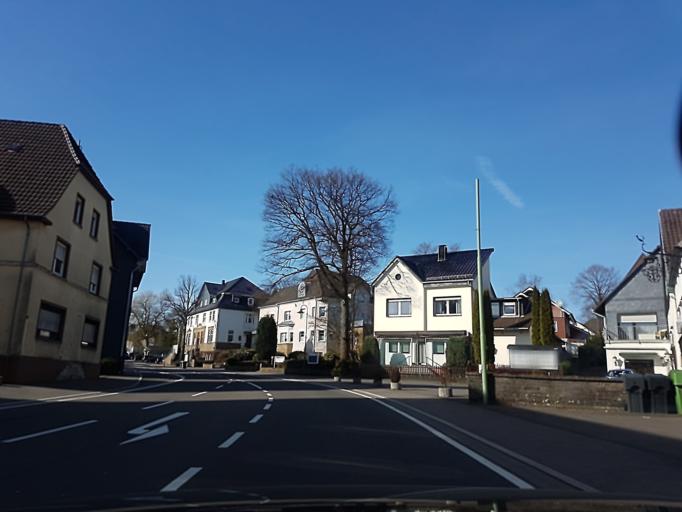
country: DE
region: North Rhine-Westphalia
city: Kierspe
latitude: 51.1374
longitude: 7.5871
